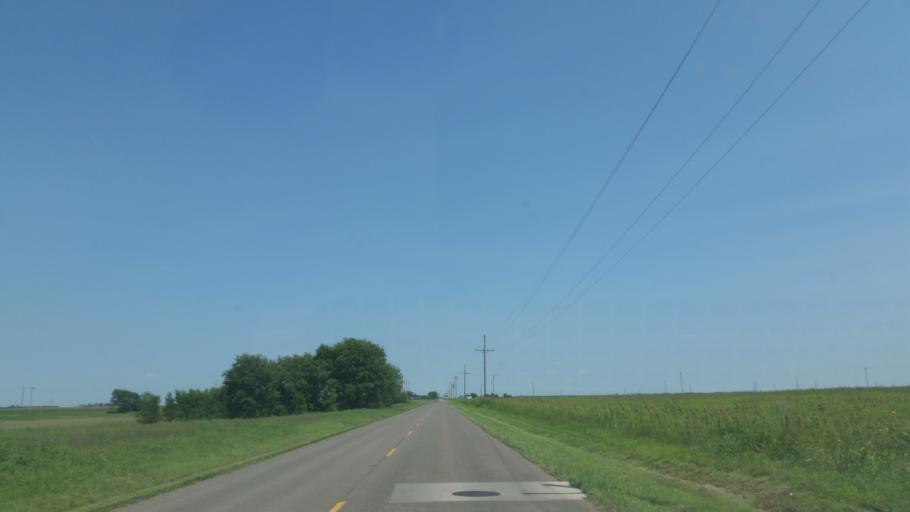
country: US
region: New Mexico
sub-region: Curry County
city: Clovis
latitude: 34.4338
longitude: -103.1645
